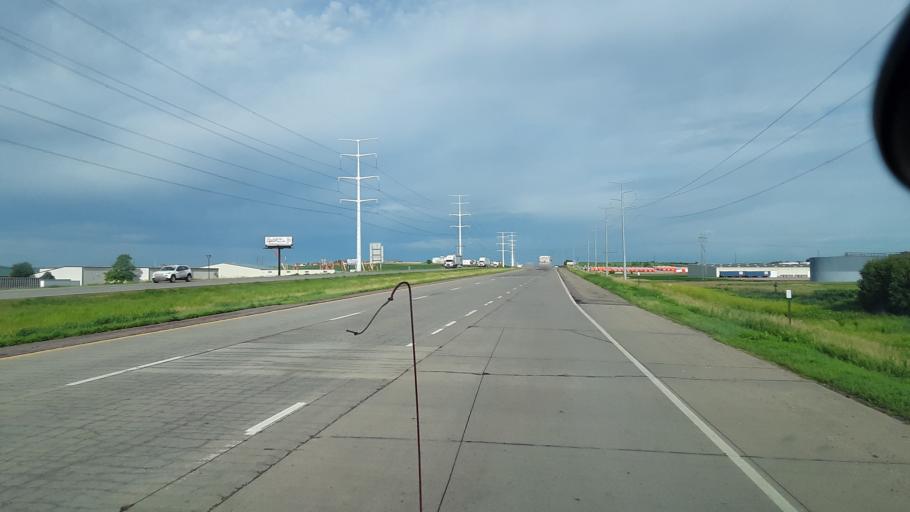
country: US
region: South Dakota
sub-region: Minnehaha County
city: Brandon
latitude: 43.6089
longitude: -96.5757
